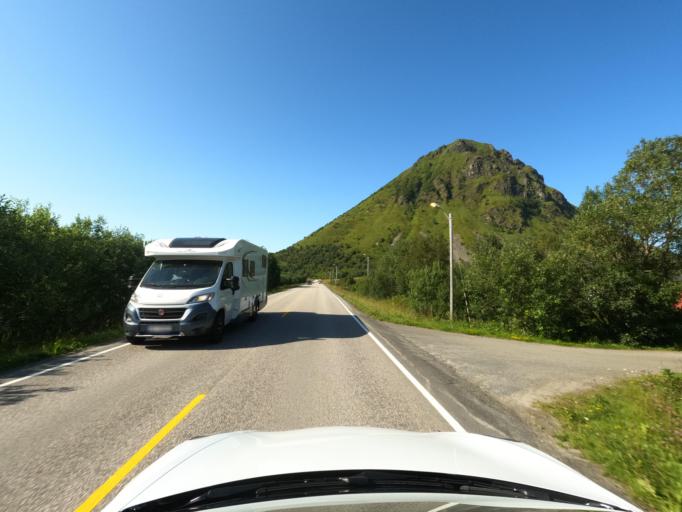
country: NO
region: Nordland
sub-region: Vestvagoy
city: Evjen
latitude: 68.2712
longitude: 13.9716
